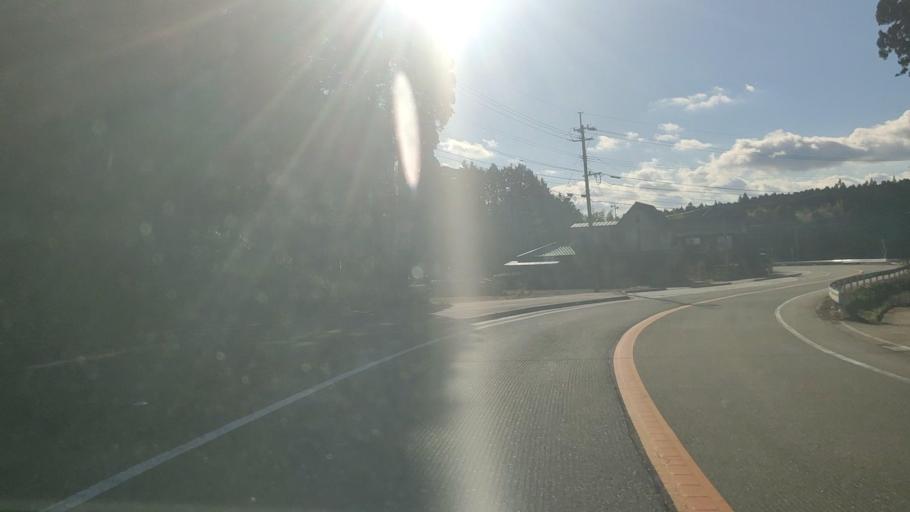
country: JP
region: Fukuoka
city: Maebaru-chuo
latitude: 33.4448
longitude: 130.2707
